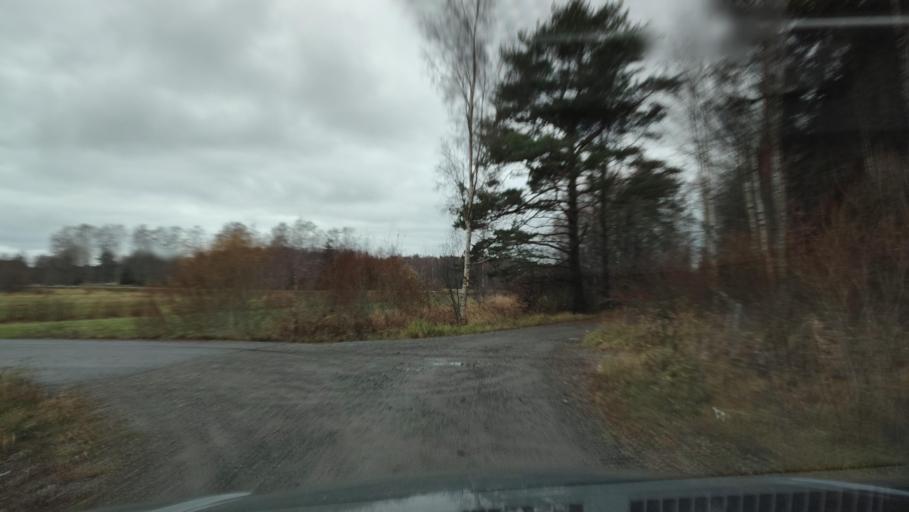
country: FI
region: Ostrobothnia
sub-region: Sydosterbotten
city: Kristinestad
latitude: 62.2794
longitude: 21.4109
